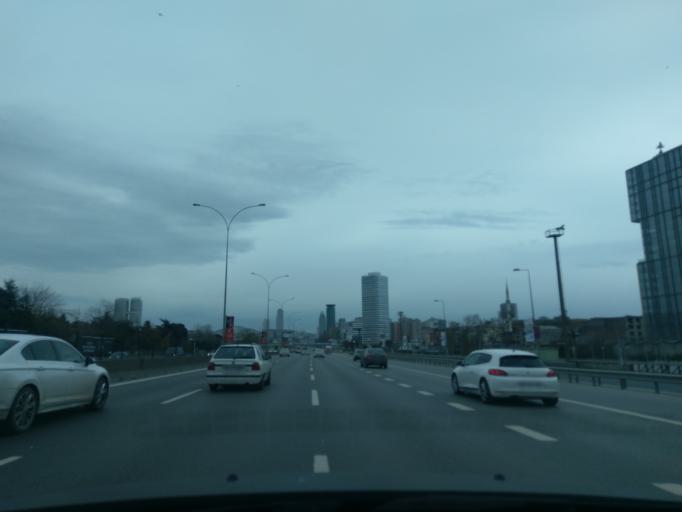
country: TR
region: Istanbul
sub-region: Atasehir
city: Atasehir
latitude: 40.9948
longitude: 29.0671
